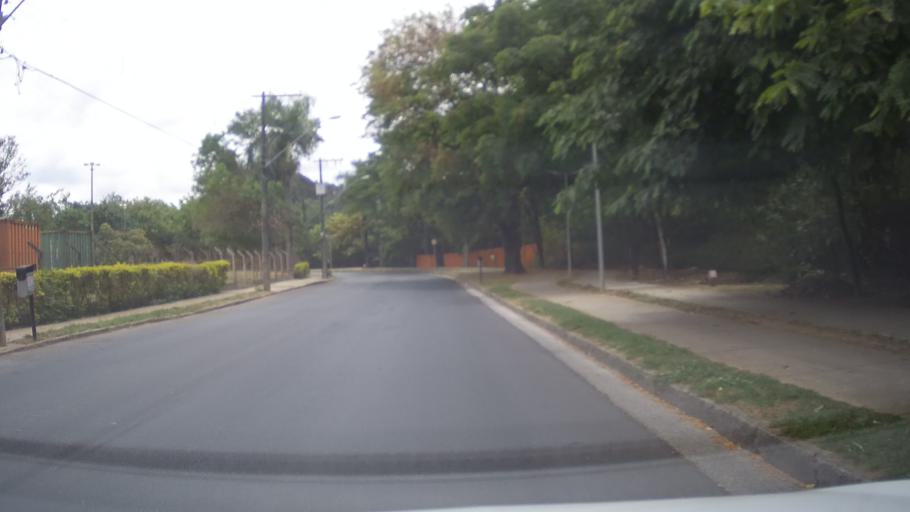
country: BR
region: Minas Gerais
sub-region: Belo Horizonte
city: Belo Horizonte
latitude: -19.8532
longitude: -43.9983
